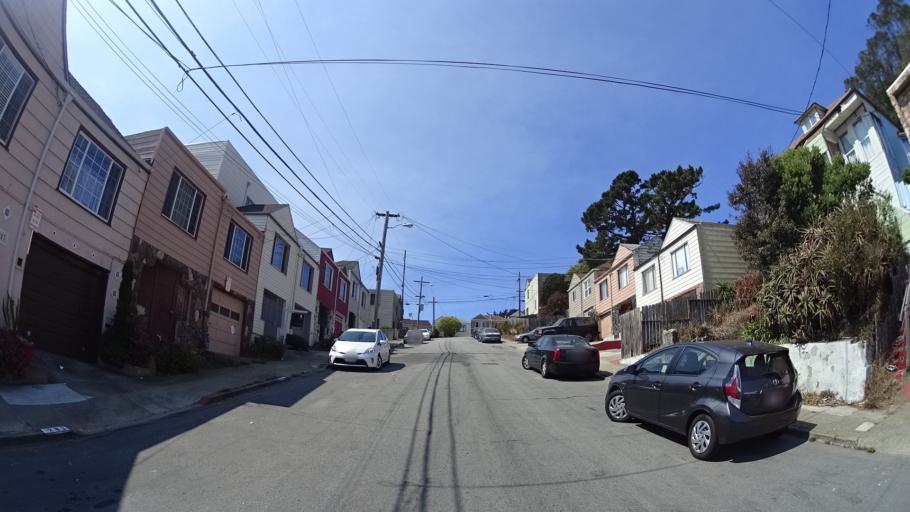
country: US
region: California
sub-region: San Mateo County
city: Daly City
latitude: 37.7174
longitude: -122.4619
